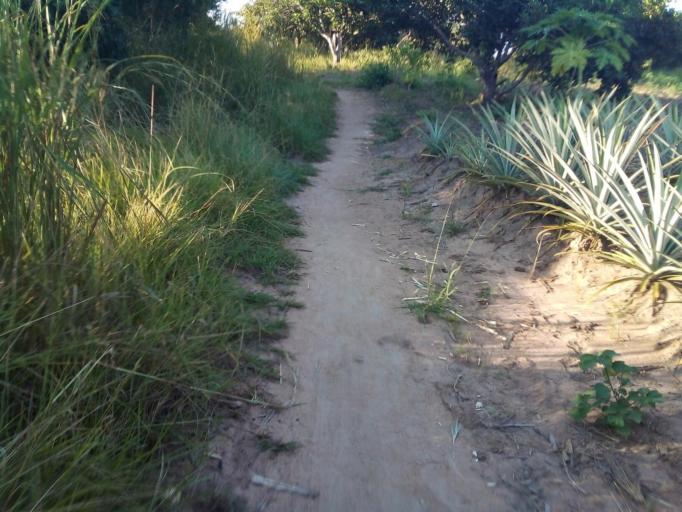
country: MZ
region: Zambezia
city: Quelimane
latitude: -17.4858
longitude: 36.8121
